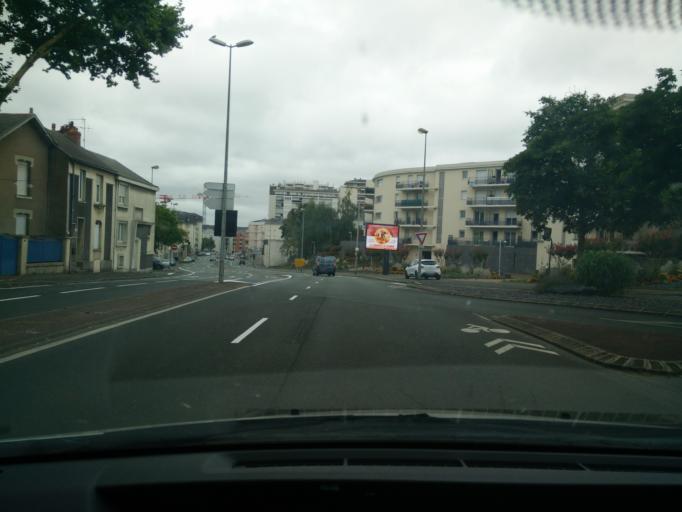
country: FR
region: Pays de la Loire
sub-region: Departement de Maine-et-Loire
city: Angers
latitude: 47.4717
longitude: -0.5386
